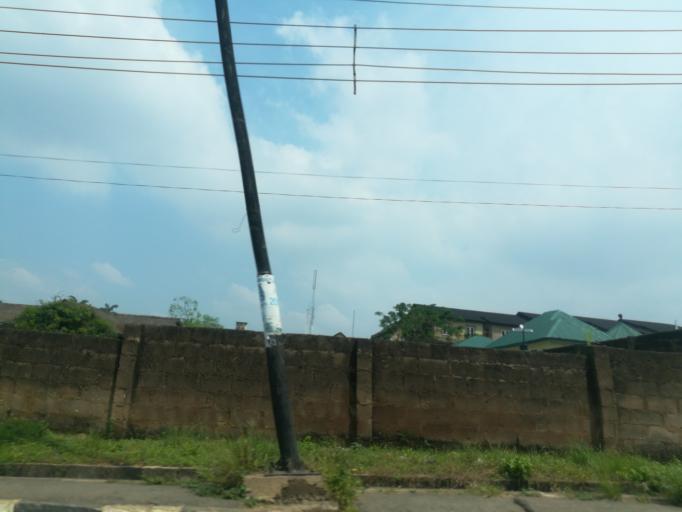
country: NG
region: Oyo
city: Ibadan
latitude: 7.3980
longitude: 3.9127
